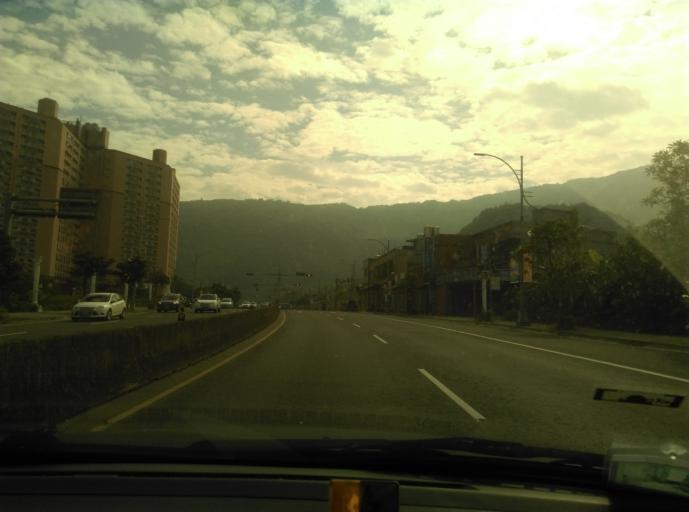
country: TW
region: Taiwan
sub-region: Keelung
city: Keelung
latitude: 25.1903
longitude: 121.6834
